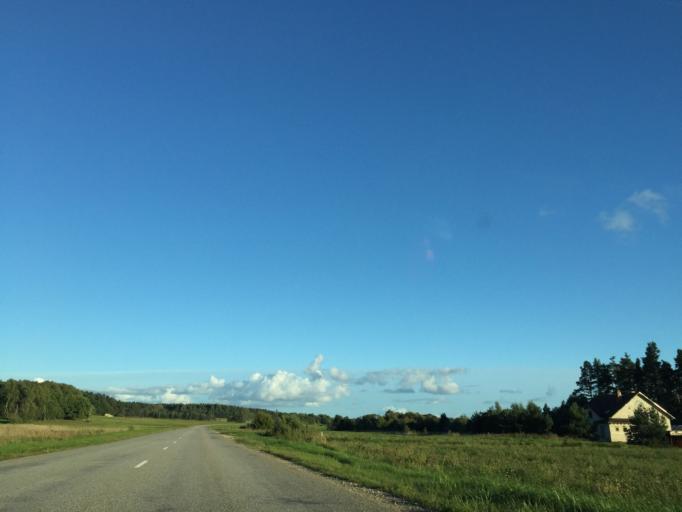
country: LV
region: Kuldigas Rajons
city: Kuldiga
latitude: 56.9308
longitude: 22.0418
